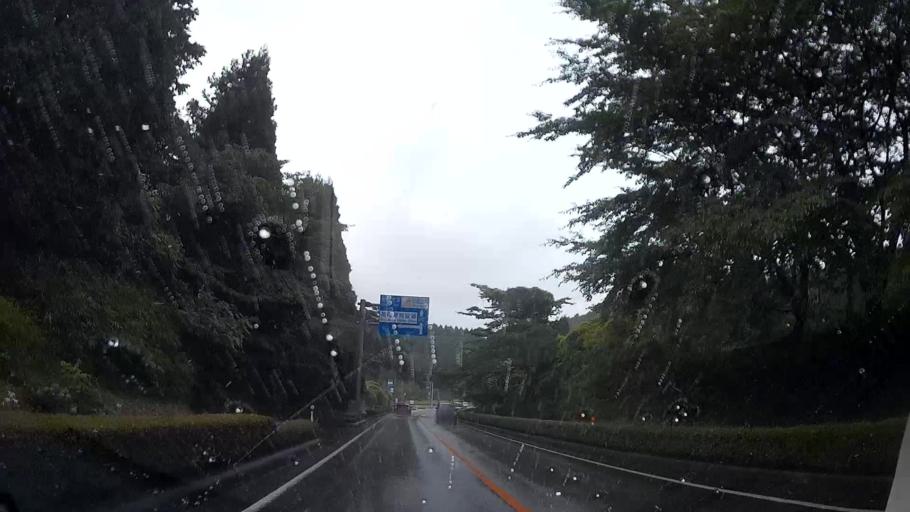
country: JP
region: Kumamoto
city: Aso
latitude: 32.8636
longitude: 131.0010
